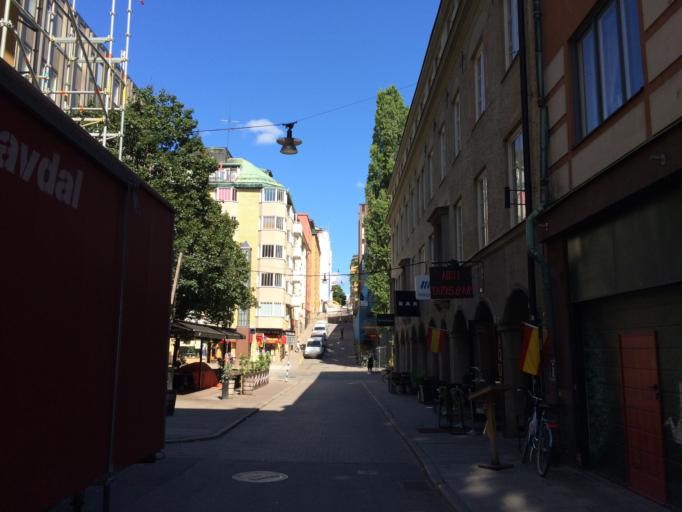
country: SE
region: Stockholm
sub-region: Stockholms Kommun
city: Stockholm
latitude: 59.3389
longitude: 18.0611
